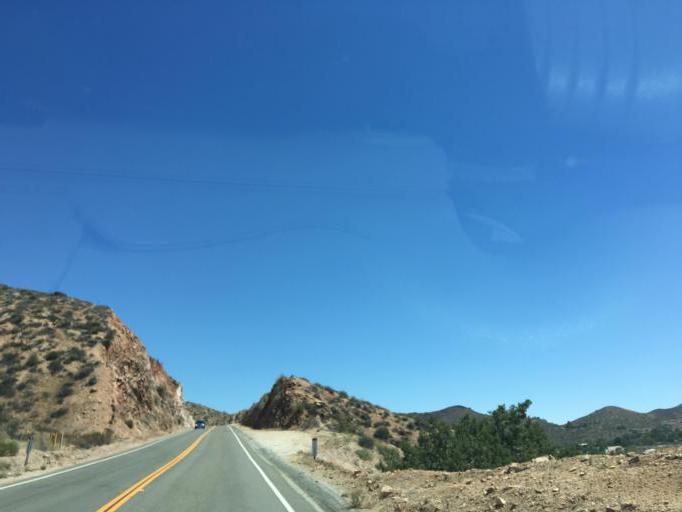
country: US
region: California
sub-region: Los Angeles County
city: Acton
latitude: 34.4547
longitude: -118.2004
